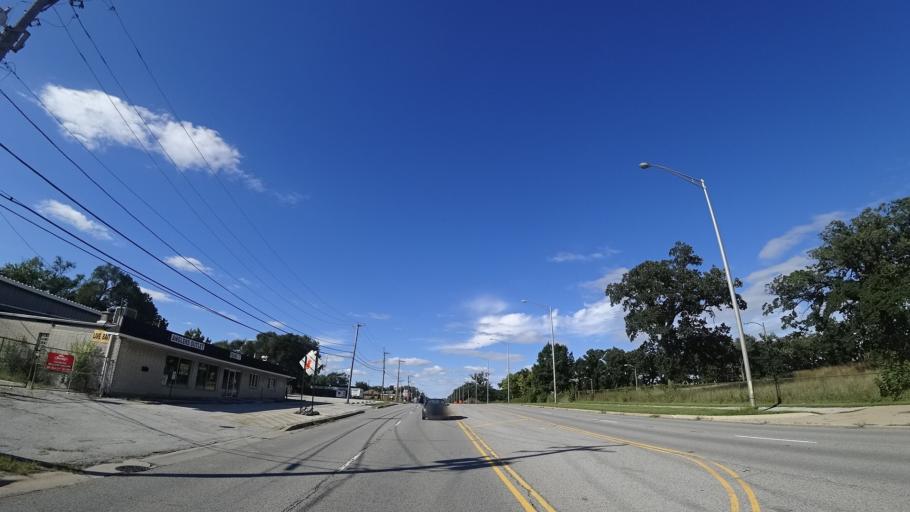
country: US
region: Illinois
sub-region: Cook County
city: Oak Forest
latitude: 41.5963
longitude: -87.7363
